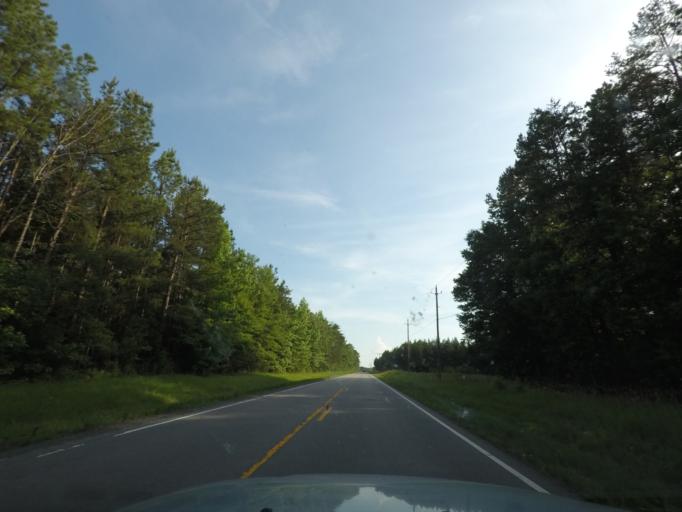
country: US
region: North Carolina
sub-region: Granville County
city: Oxford
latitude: 36.4223
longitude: -78.5849
